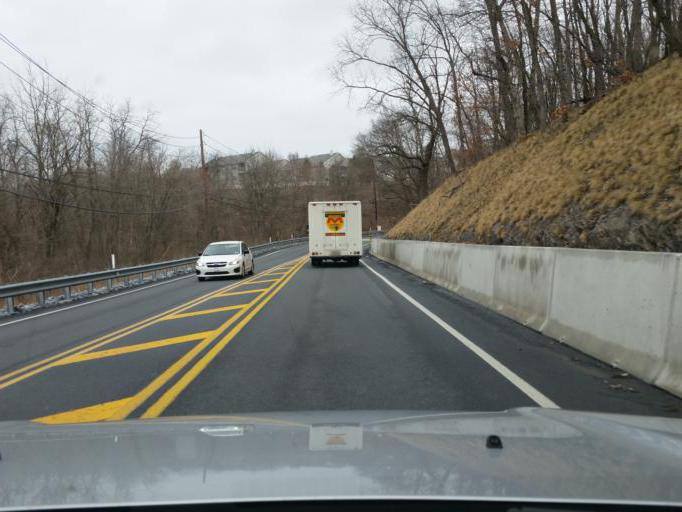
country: US
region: Pennsylvania
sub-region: Dauphin County
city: Rutherford
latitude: 40.2961
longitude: -76.7683
